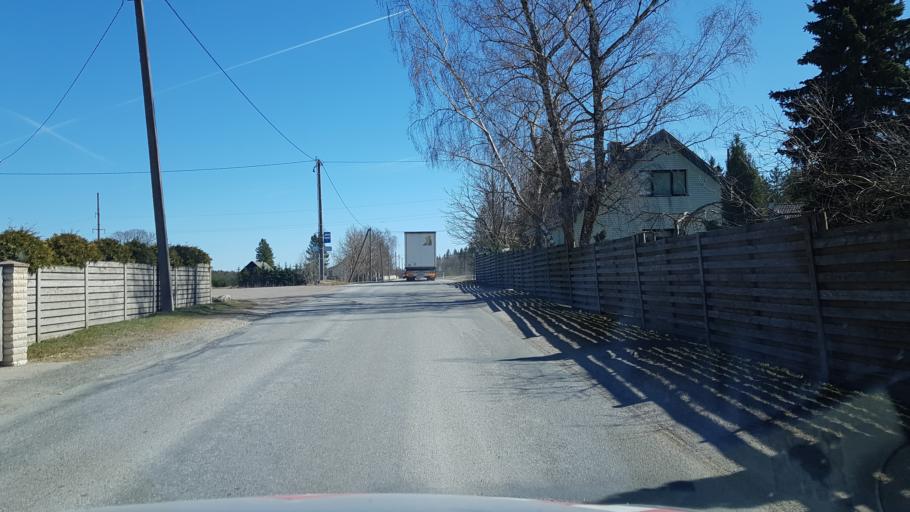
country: EE
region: Laeaene-Virumaa
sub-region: Rakvere linn
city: Rakvere
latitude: 59.3368
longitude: 26.3899
